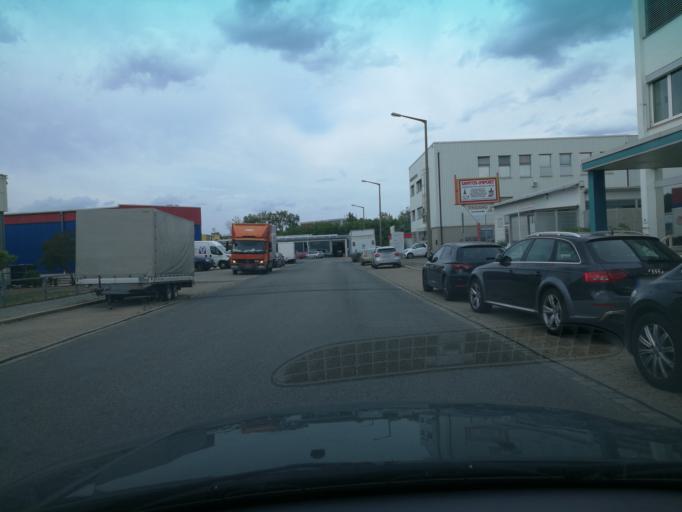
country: DE
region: Bavaria
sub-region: Regierungsbezirk Mittelfranken
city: Nuernberg
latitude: 49.4707
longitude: 11.0750
